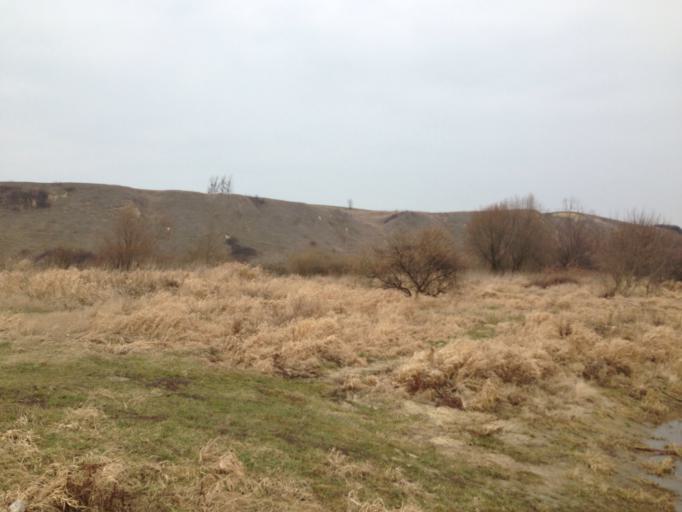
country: PL
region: Pomeranian Voivodeship
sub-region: Powiat tczewski
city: Gniew
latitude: 53.8340
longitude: 18.8369
